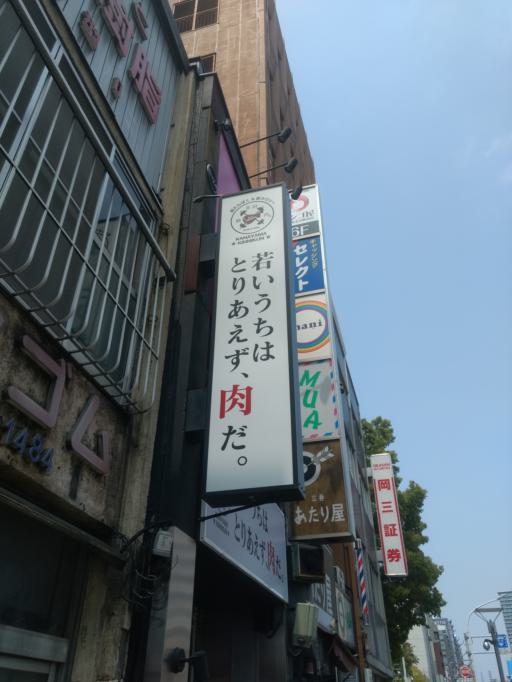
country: JP
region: Aichi
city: Nagoya-shi
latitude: 35.1446
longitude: 136.9028
